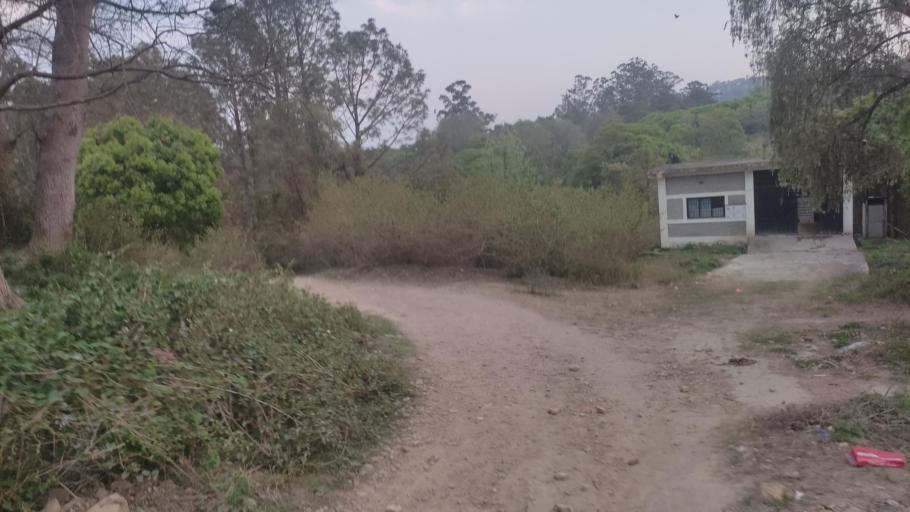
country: NP
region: Central Region
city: Kirtipur
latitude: 27.6814
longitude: 85.2877
